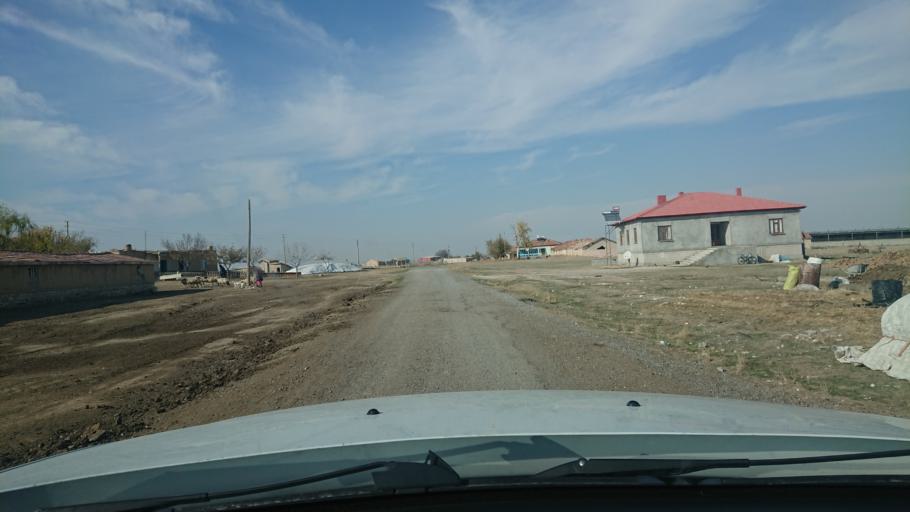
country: TR
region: Aksaray
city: Sultanhani
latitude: 38.2562
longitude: 33.4782
